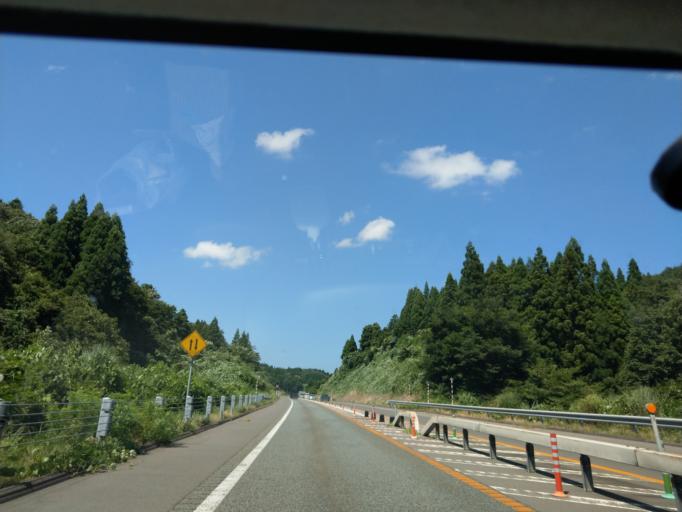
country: JP
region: Akita
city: Akita
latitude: 39.6717
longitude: 140.1878
